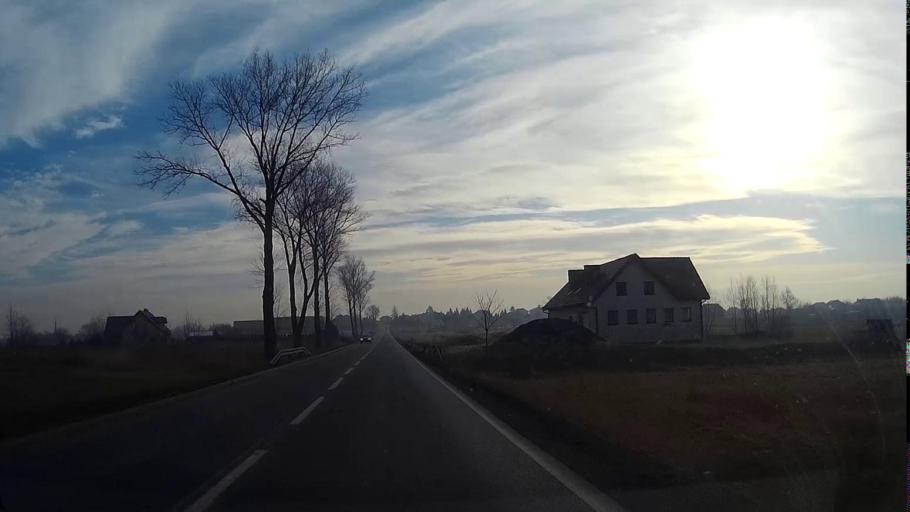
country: PL
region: Lesser Poland Voivodeship
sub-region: Powiat krakowski
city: Liszki
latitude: 50.0362
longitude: 19.7485
